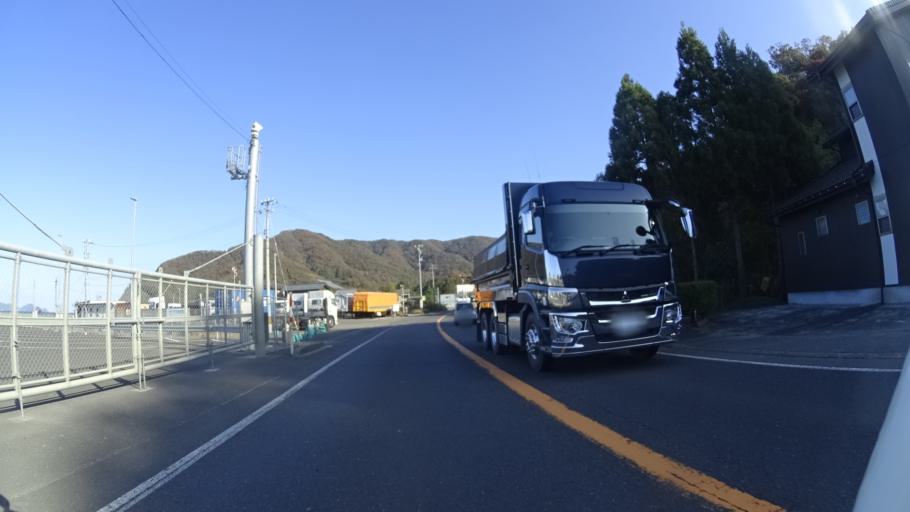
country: JP
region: Fukui
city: Tsuruga
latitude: 35.6817
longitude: 136.0855
